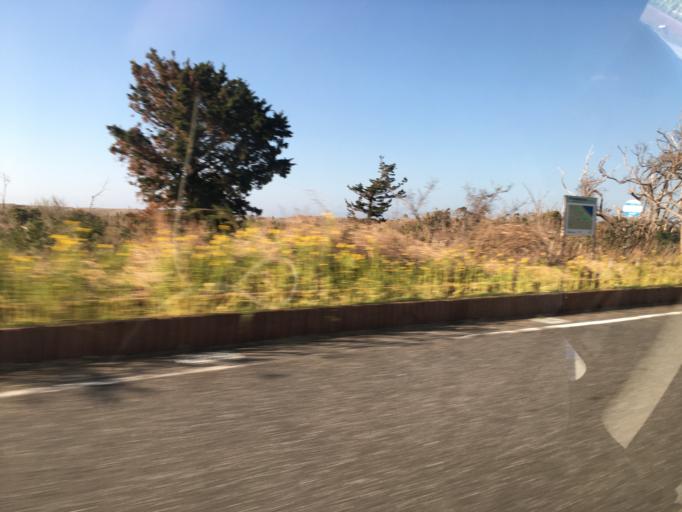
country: JP
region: Chiba
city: Tateyama
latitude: 34.9487
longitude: 139.8075
